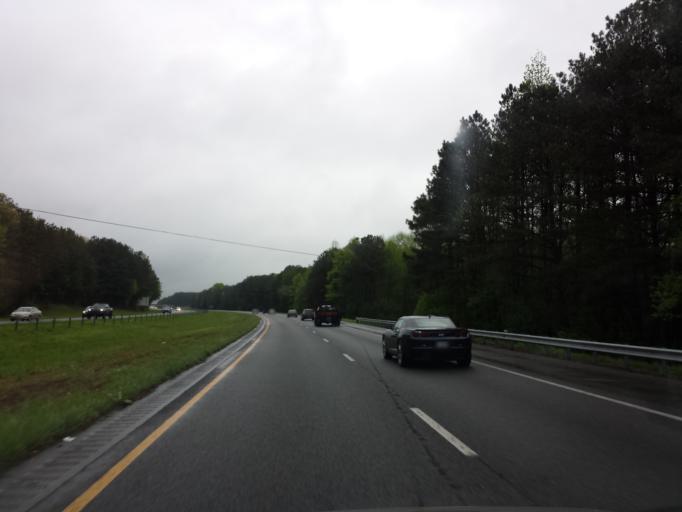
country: US
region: Georgia
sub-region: Cherokee County
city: Holly Springs
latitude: 34.2024
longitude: -84.4952
